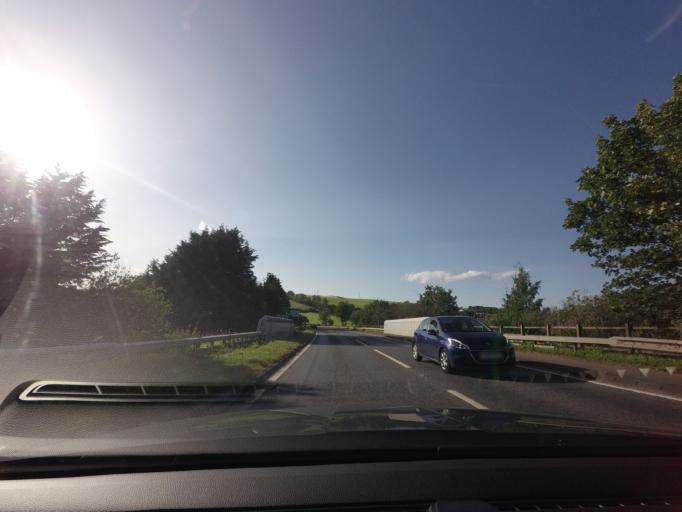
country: GB
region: Scotland
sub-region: Highland
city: Conon Bridge
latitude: 57.5778
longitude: -4.4351
